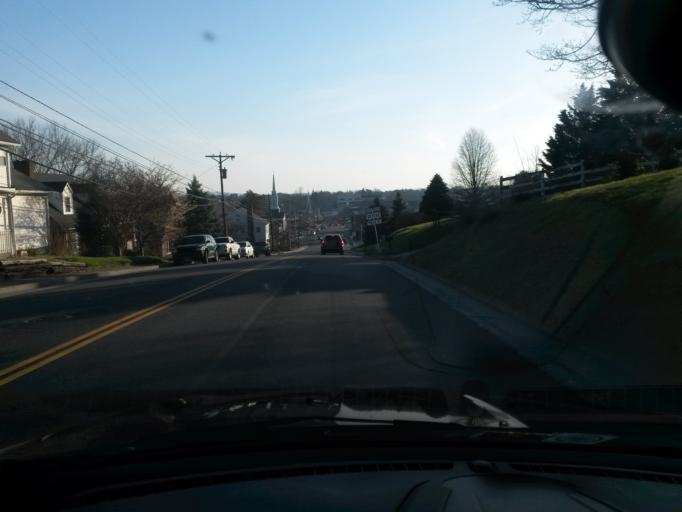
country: US
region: Virginia
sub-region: Montgomery County
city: Christiansburg
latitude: 37.1253
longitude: -80.4142
